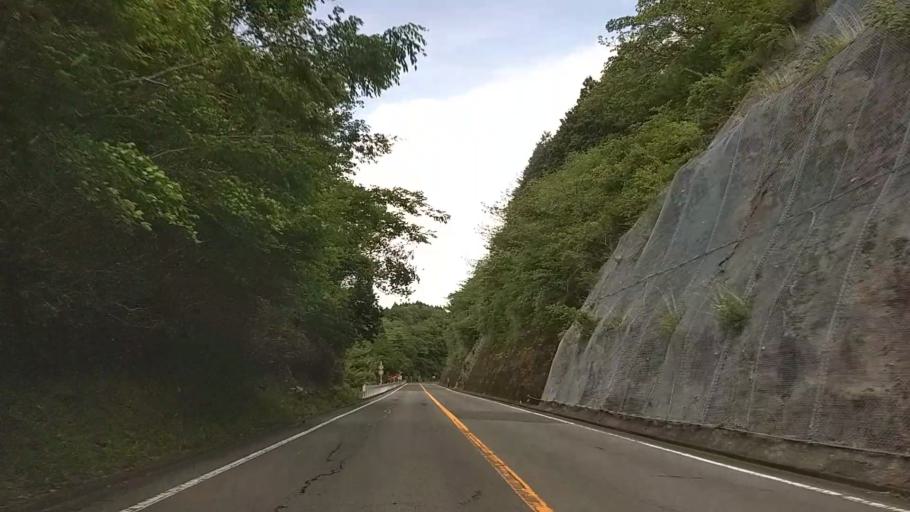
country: JP
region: Kanagawa
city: Odawara
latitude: 35.2134
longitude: 139.1037
